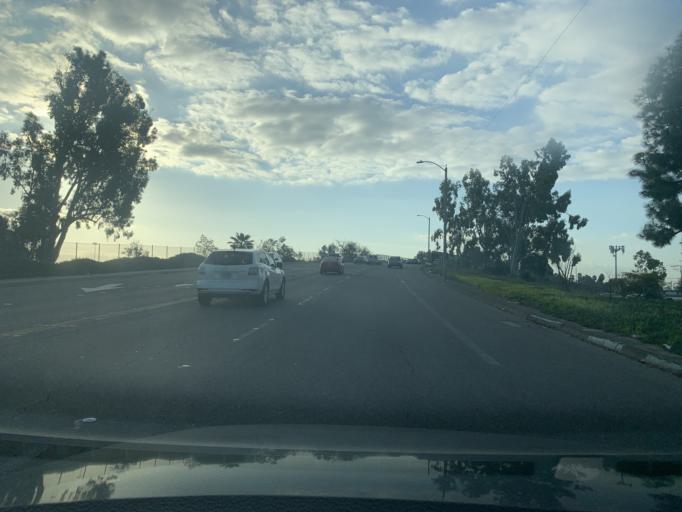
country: US
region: California
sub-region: Orange County
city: Westminster
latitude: 33.7550
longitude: -118.0157
